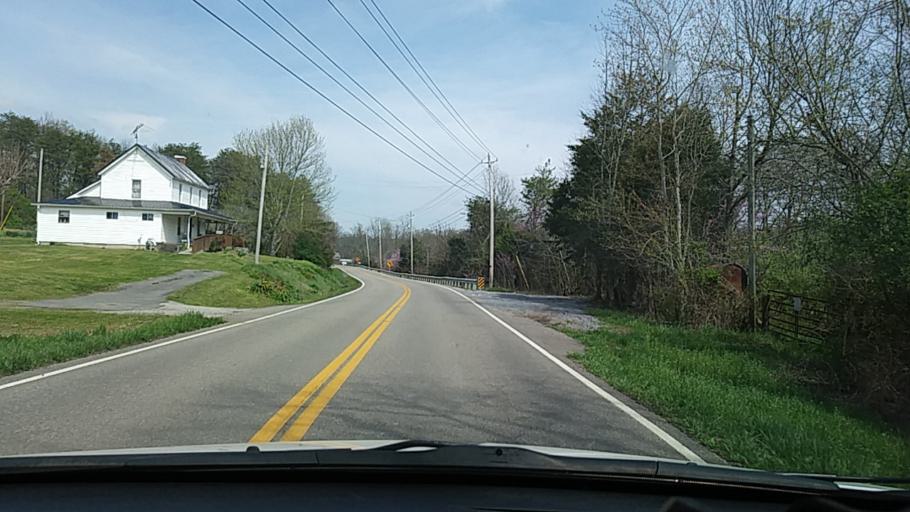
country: US
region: Tennessee
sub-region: Greene County
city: Greeneville
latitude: 36.0890
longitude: -82.7996
